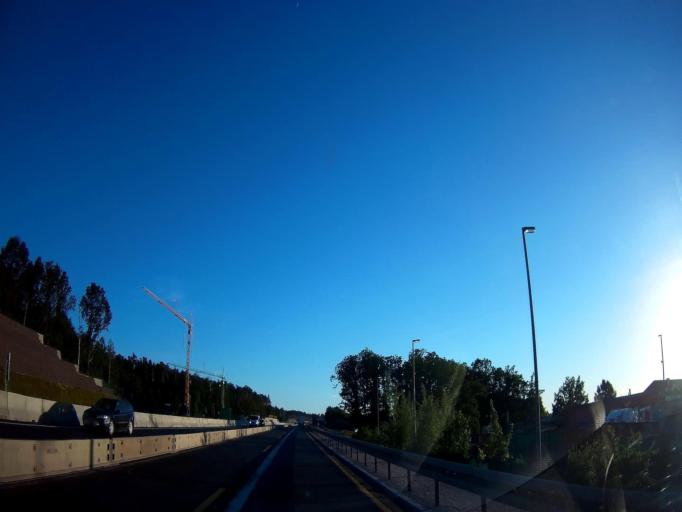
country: DE
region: Bavaria
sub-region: Regierungsbezirk Mittelfranken
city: Schwabach
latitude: 49.3191
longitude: 11.0411
